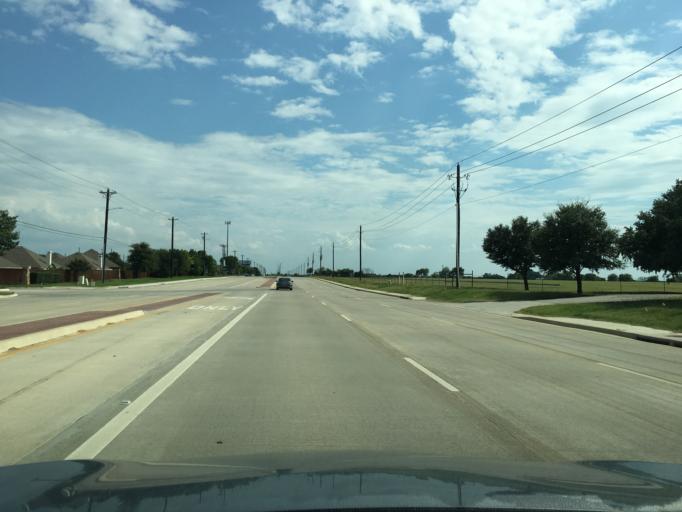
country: US
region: Texas
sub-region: Denton County
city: Oak Point
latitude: 33.1783
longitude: -96.9771
